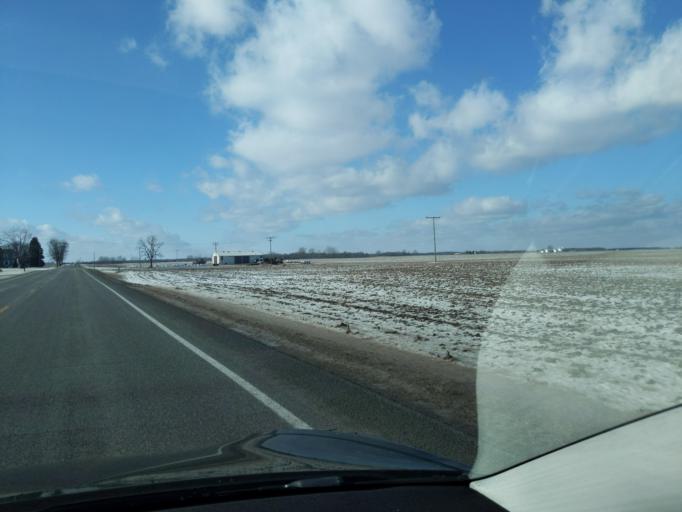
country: US
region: Michigan
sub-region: Ingham County
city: Williamston
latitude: 42.6010
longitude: -84.2869
